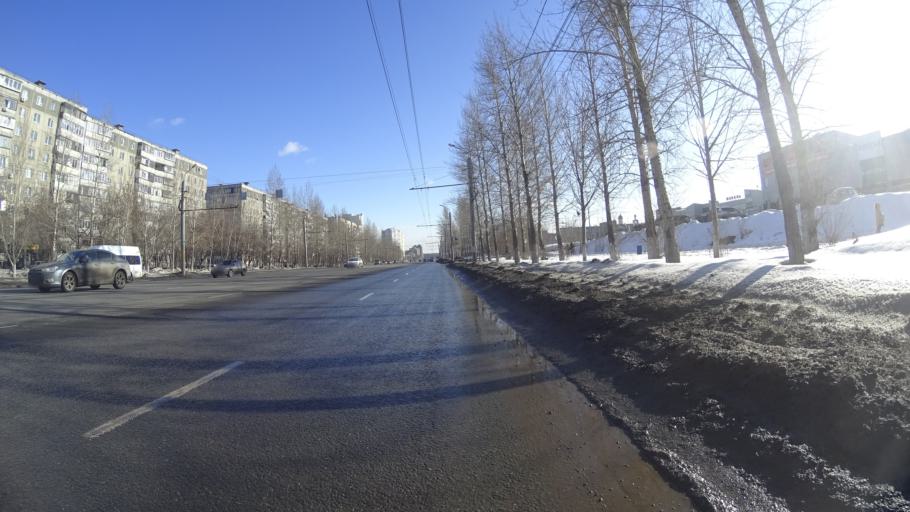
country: RU
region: Chelyabinsk
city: Roshchino
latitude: 55.1862
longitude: 61.2874
